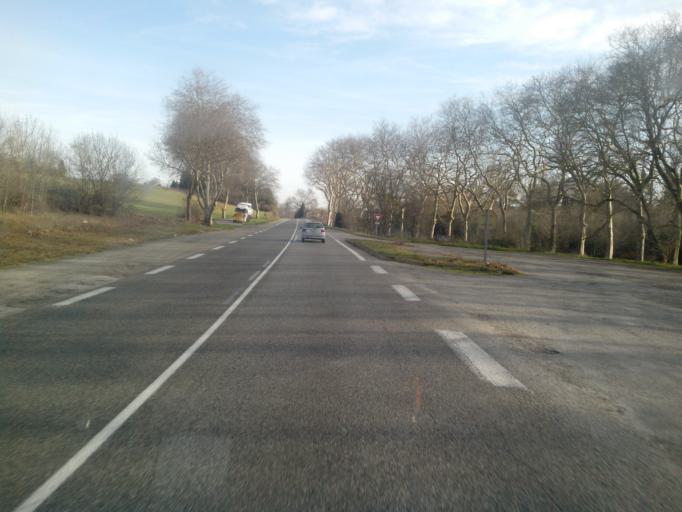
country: FR
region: Languedoc-Roussillon
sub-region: Departement de l'Aude
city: Saint-Martin-Lalande
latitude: 43.2993
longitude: 1.9893
